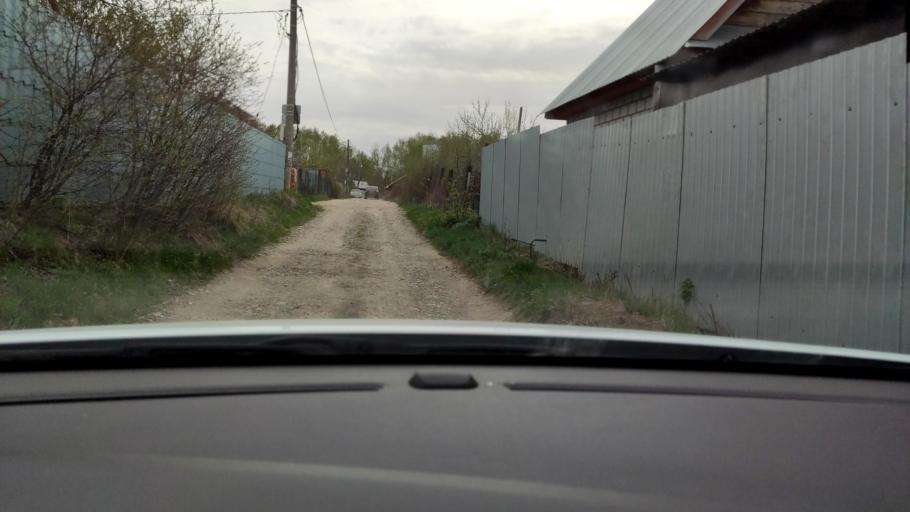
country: RU
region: Tatarstan
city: Vysokaya Gora
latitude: 55.8137
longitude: 49.2806
